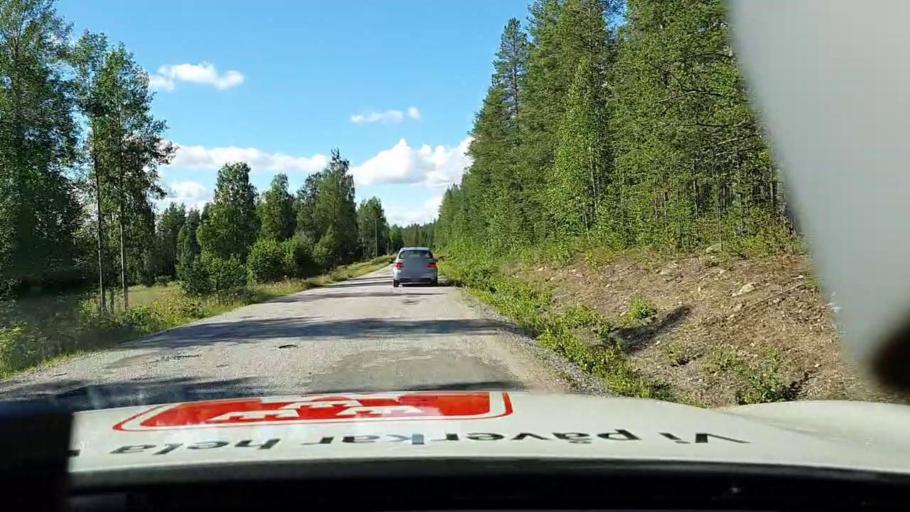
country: SE
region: Norrbotten
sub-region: Overkalix Kommun
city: OEverkalix
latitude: 66.2526
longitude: 23.1262
